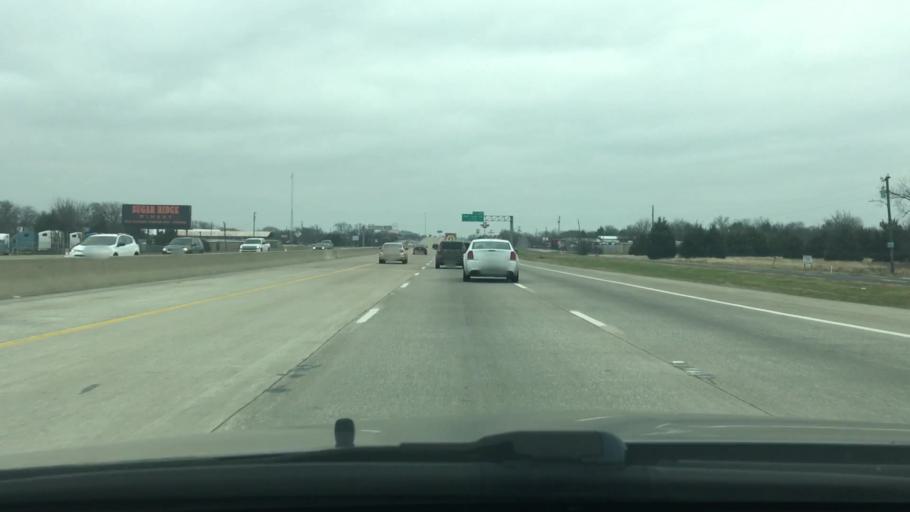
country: US
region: Texas
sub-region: Dallas County
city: Wilmer
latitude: 32.6027
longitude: -96.6854
